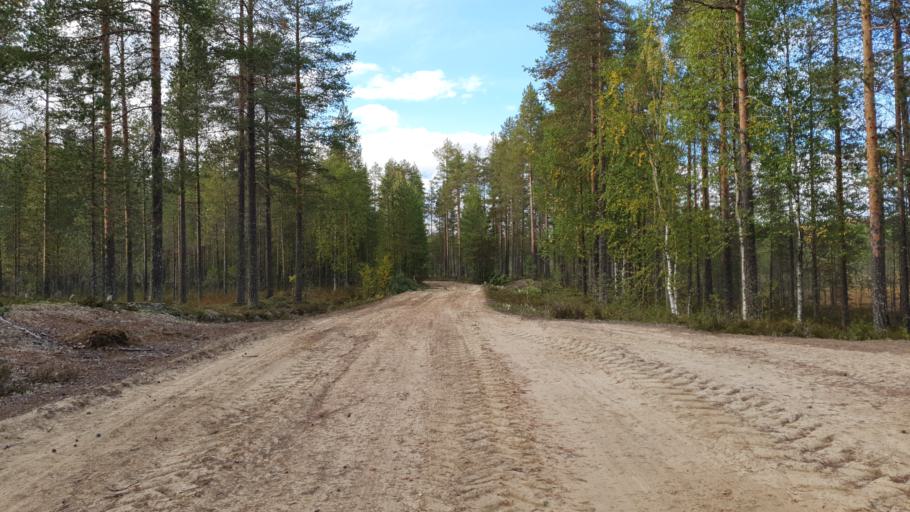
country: FI
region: Kainuu
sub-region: Kehys-Kainuu
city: Kuhmo
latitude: 64.2023
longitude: 29.1676
